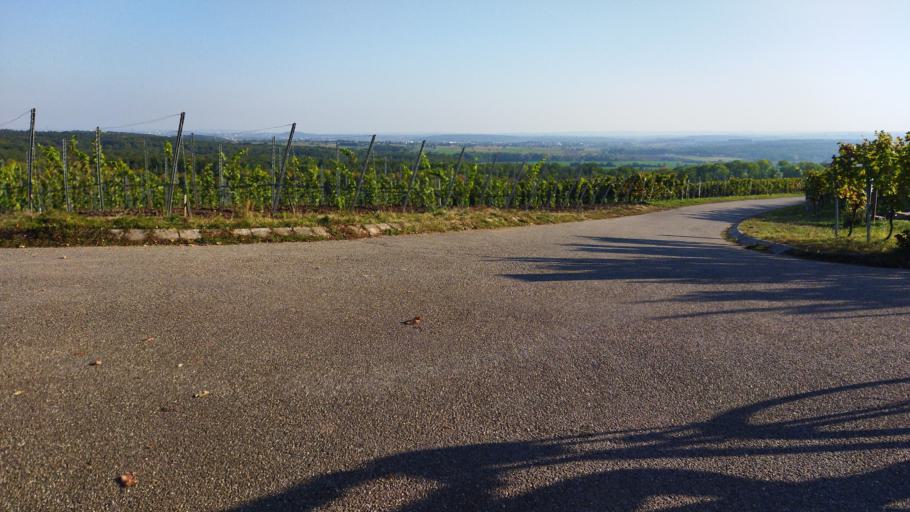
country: DE
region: Baden-Wuerttemberg
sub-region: Regierungsbezirk Stuttgart
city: Freudental
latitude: 49.0048
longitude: 9.0518
